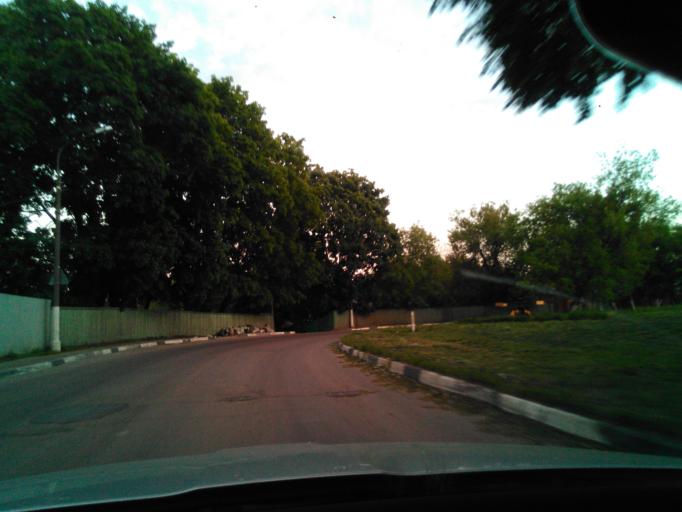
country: RU
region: Moskovskaya
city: Dolgoprudnyy
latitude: 55.9521
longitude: 37.5071
